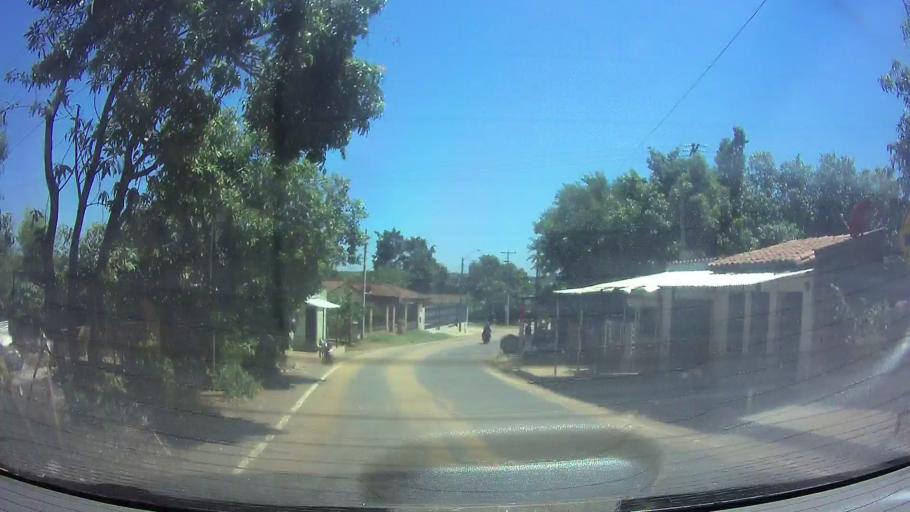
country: PY
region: Central
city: San Lorenzo
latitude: -25.3298
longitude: -57.4863
